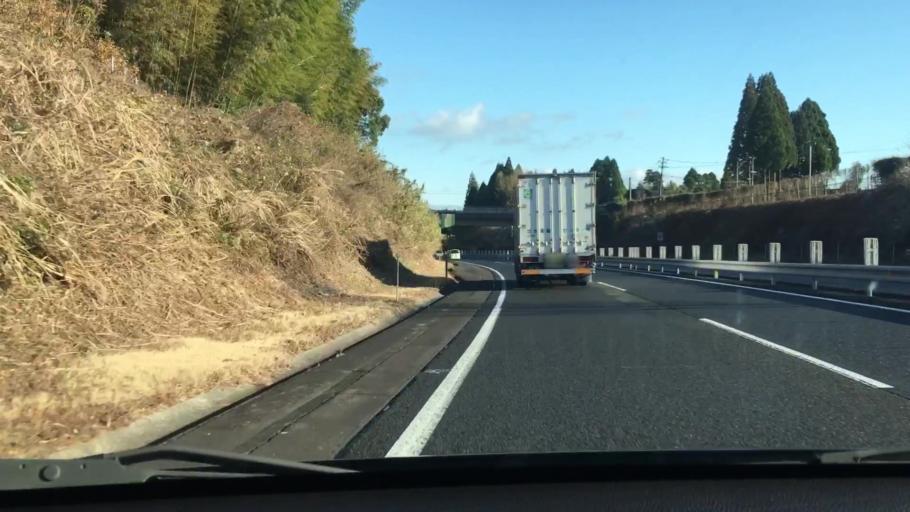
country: JP
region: Kagoshima
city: Kajiki
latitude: 31.8204
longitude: 130.6966
